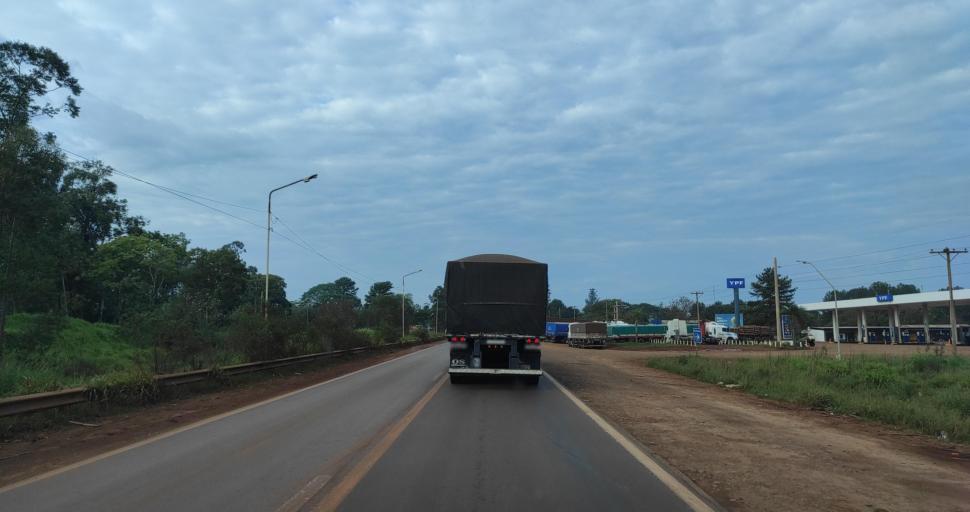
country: AR
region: Corrientes
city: Gobernador Ingeniero Valentin Virasoro
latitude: -28.0243
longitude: -56.0150
